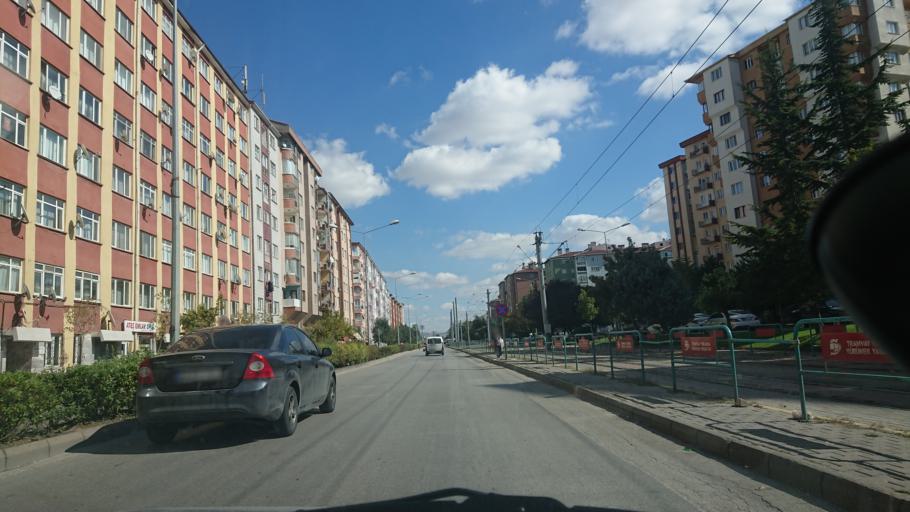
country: TR
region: Eskisehir
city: Eskisehir
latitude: 39.7653
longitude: 30.5518
